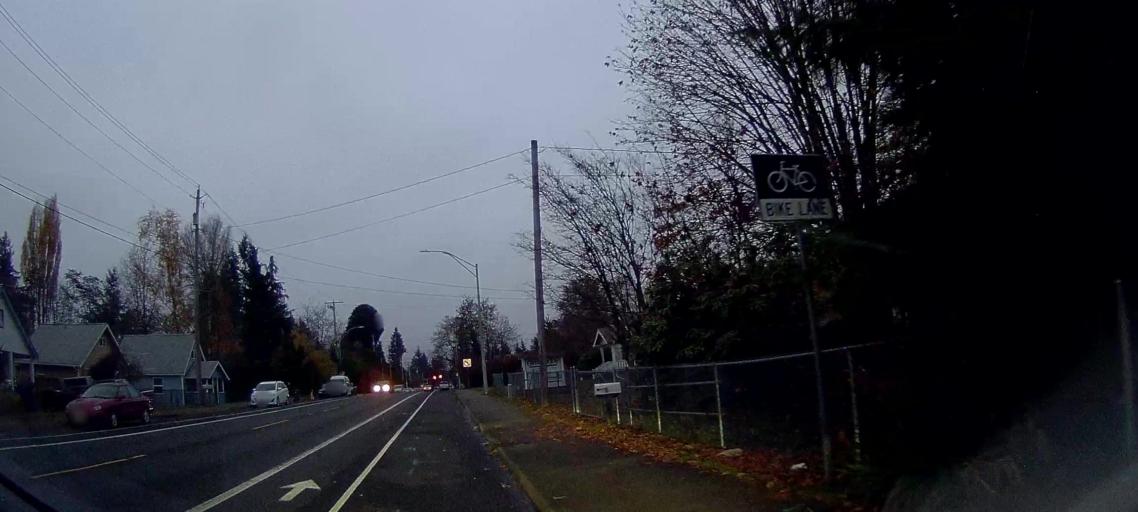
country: US
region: Washington
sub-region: Thurston County
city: Olympia
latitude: 47.0427
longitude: -122.8691
